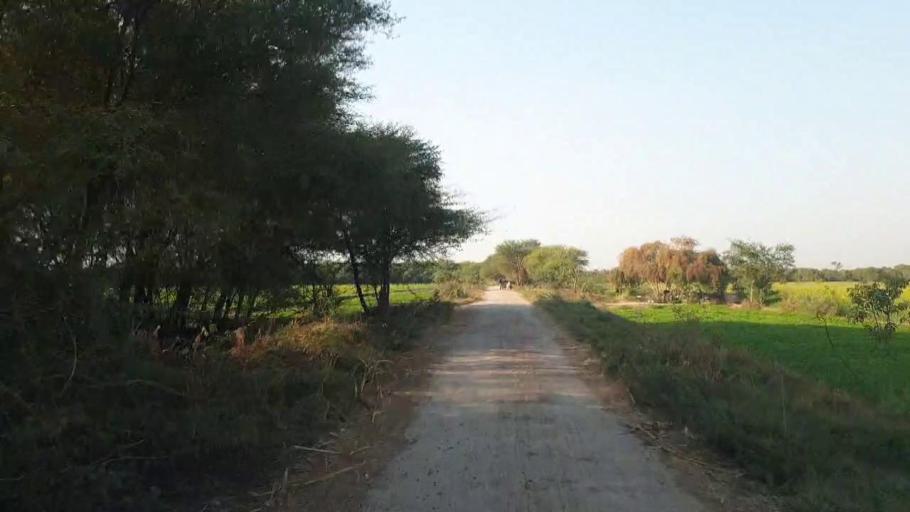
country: PK
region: Sindh
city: Mirpur Khas
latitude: 25.4334
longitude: 68.9109
